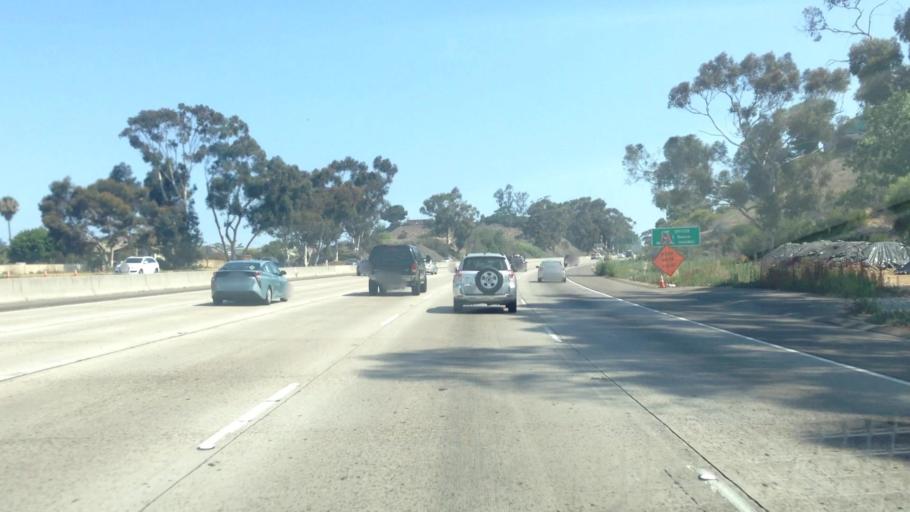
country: US
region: California
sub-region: San Diego County
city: San Diego
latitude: 32.7798
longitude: -117.1627
